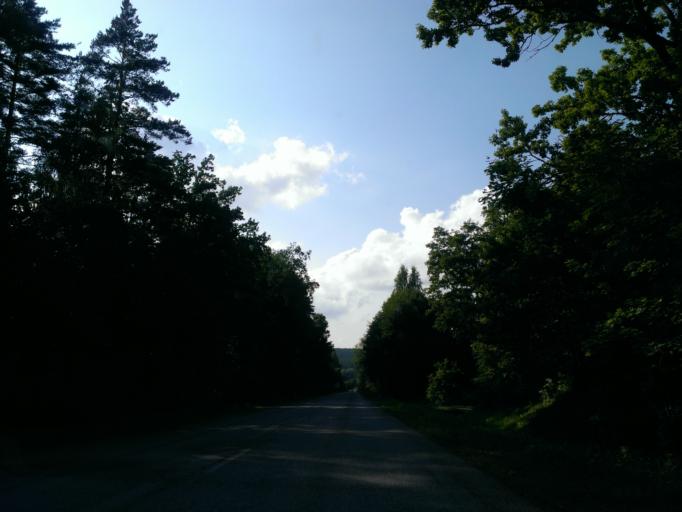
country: LV
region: Priekuli
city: Priekuli
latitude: 57.3049
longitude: 25.3986
